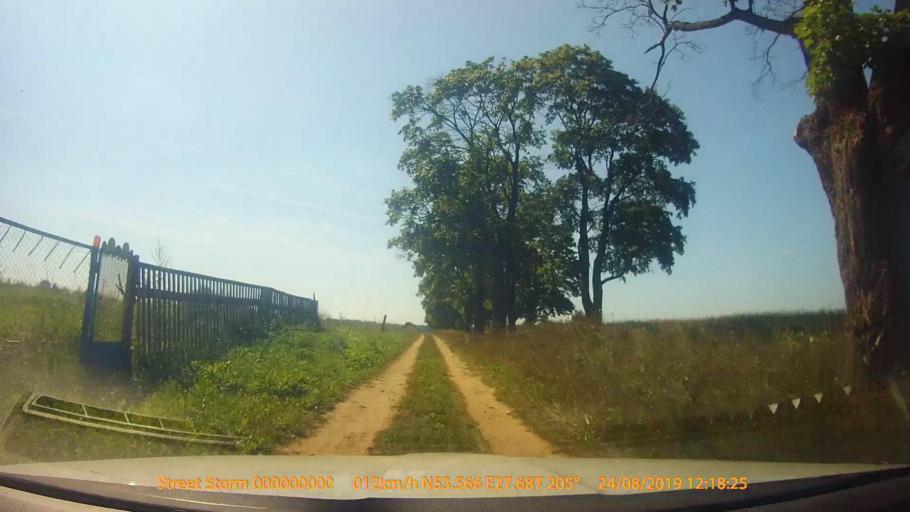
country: BY
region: Minsk
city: Prawdzinski
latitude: 53.5662
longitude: 27.6877
